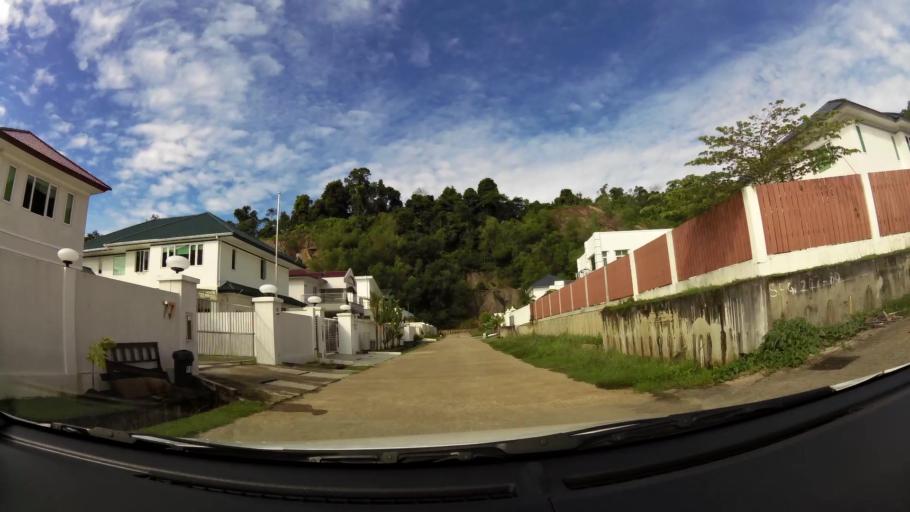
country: BN
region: Brunei and Muara
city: Bandar Seri Begawan
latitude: 4.8975
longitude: 114.9630
